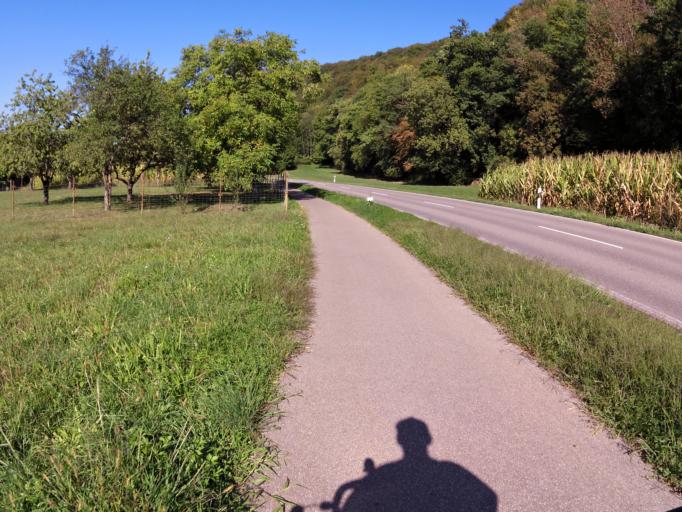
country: DE
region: Baden-Wuerttemberg
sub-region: Freiburg Region
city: Hohentengen am Hochrhein
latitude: 47.5702
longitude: 8.3642
